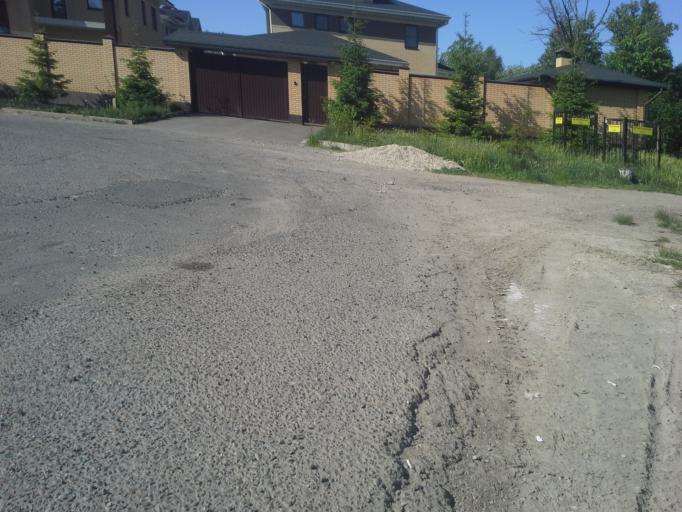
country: RU
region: Moskovskaya
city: Vatutinki
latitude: 55.4588
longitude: 37.3998
